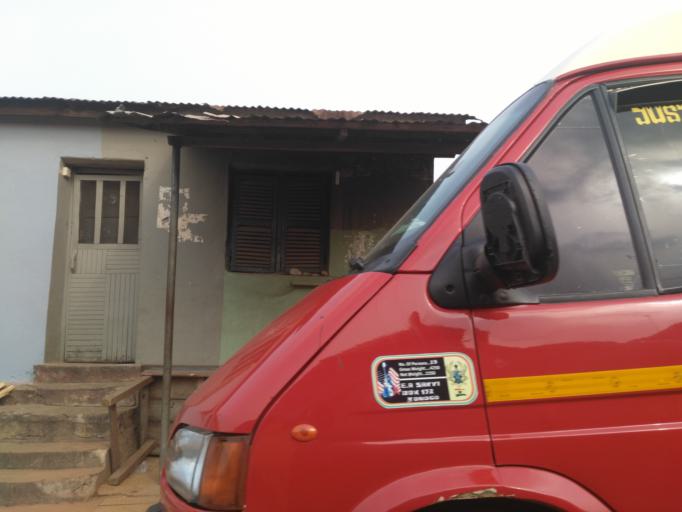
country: GH
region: Ashanti
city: Kumasi
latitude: 6.6914
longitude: -1.6150
